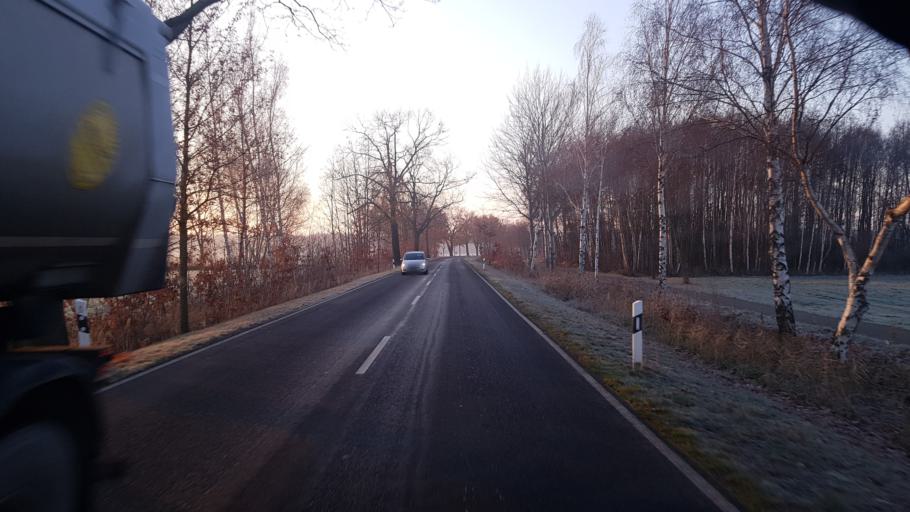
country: DE
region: Brandenburg
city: Tettau
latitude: 51.4555
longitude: 13.7391
